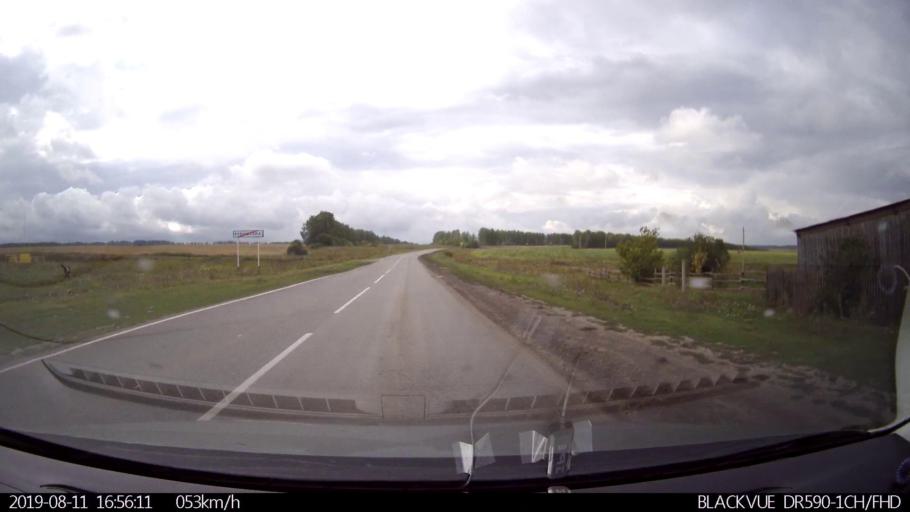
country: RU
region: Ulyanovsk
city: Mayna
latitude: 54.2860
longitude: 47.6562
